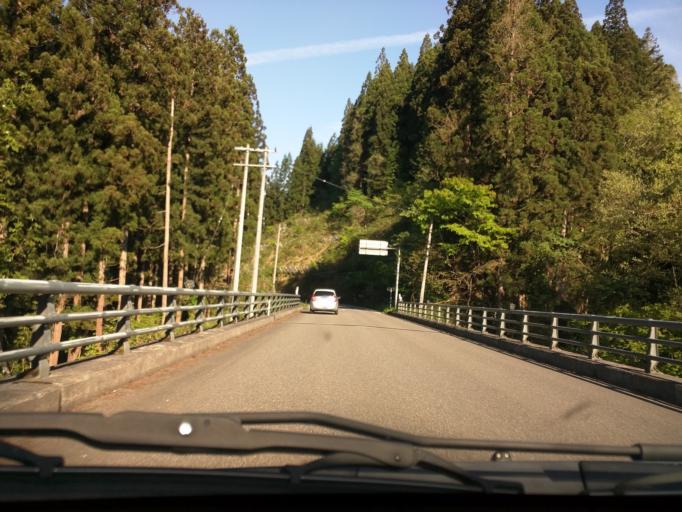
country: JP
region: Fukushima
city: Kitakata
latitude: 37.5028
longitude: 139.7327
